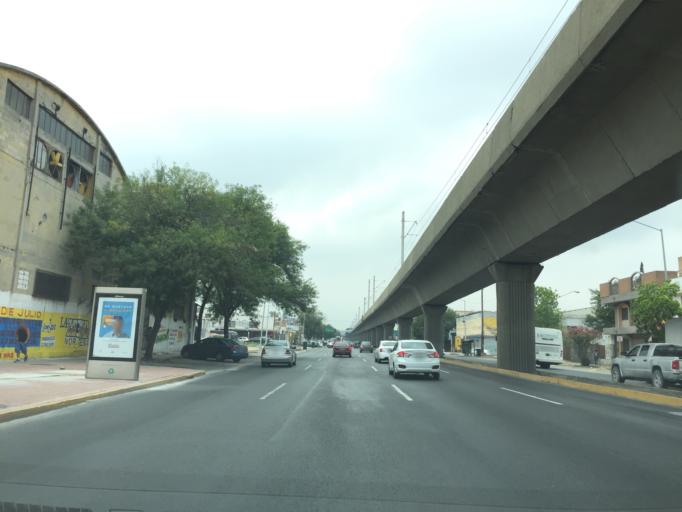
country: MX
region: Nuevo Leon
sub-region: Monterrey
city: Monterrey
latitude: 25.6842
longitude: -100.2996
